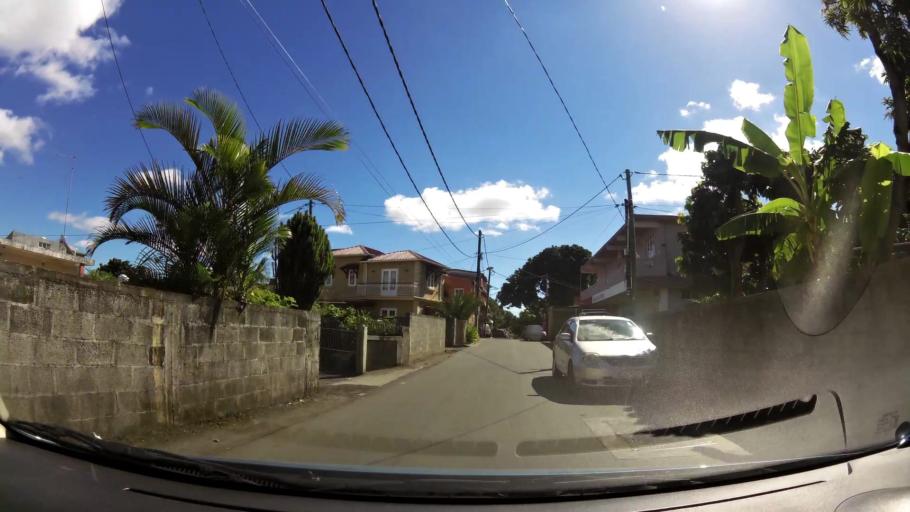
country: MU
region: Plaines Wilhems
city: Vacoas
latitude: -20.2926
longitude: 57.4798
